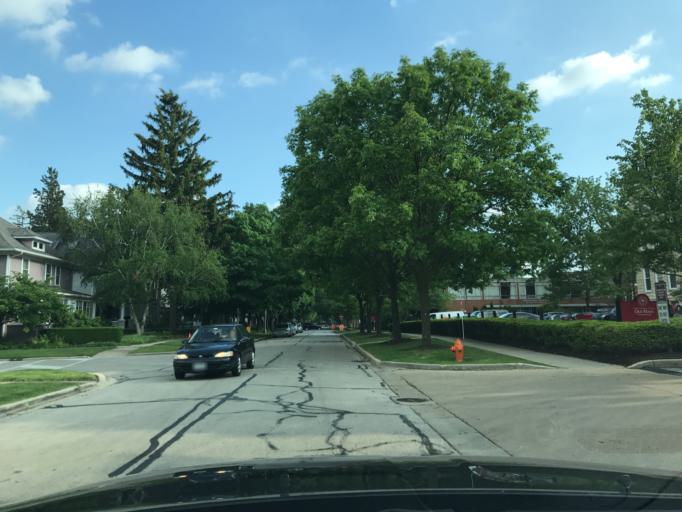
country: US
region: Illinois
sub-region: DuPage County
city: Naperville
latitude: 41.7762
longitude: -88.1423
